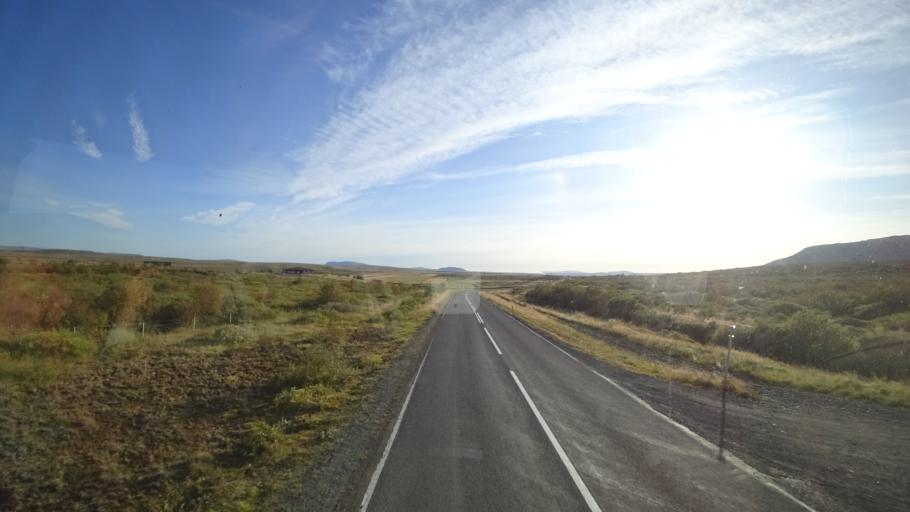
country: IS
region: South
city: Selfoss
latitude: 64.2601
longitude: -20.4730
